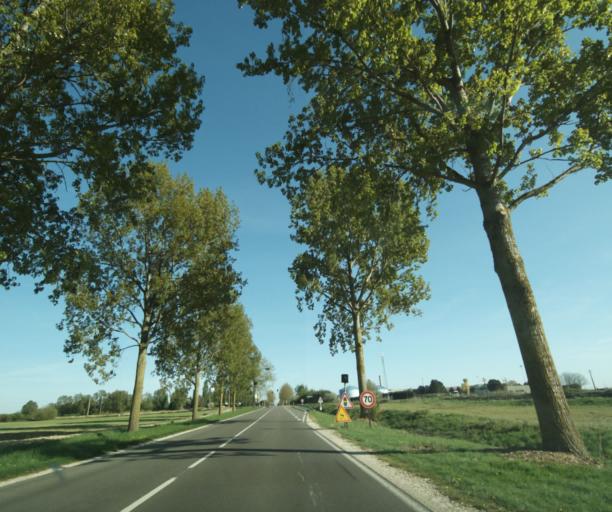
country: FR
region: Ile-de-France
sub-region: Departement de Seine-et-Marne
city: Nangis
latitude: 48.5686
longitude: 3.0037
